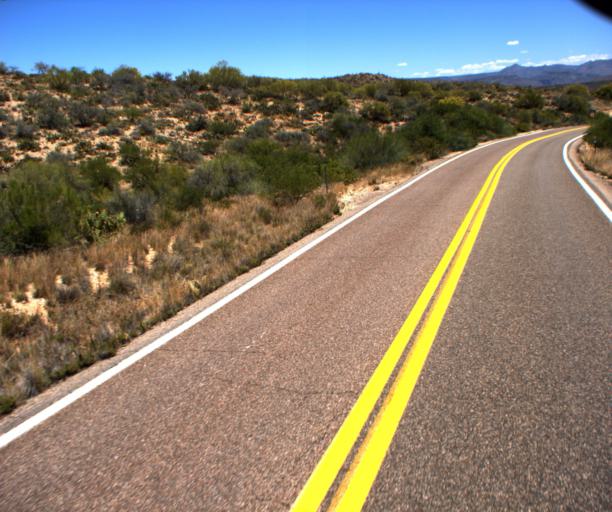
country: US
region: Arizona
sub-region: Yavapai County
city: Bagdad
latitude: 34.5224
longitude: -113.1093
